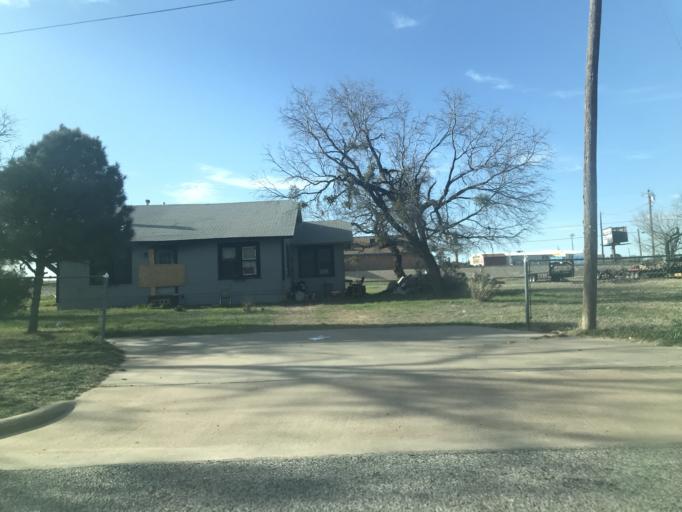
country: US
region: Texas
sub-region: Tom Green County
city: San Angelo
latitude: 31.4361
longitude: -100.4468
